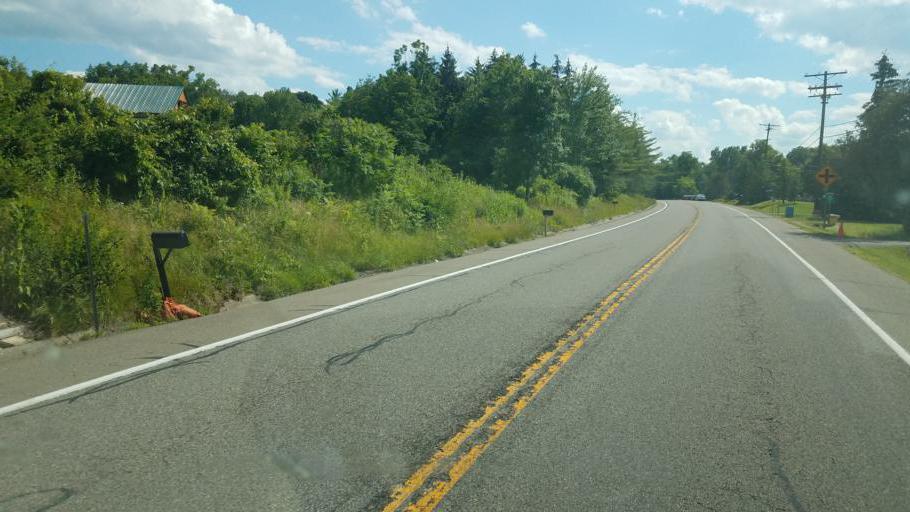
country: US
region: New York
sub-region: Steuben County
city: Sylvan Beach
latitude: 42.4751
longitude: -77.1513
